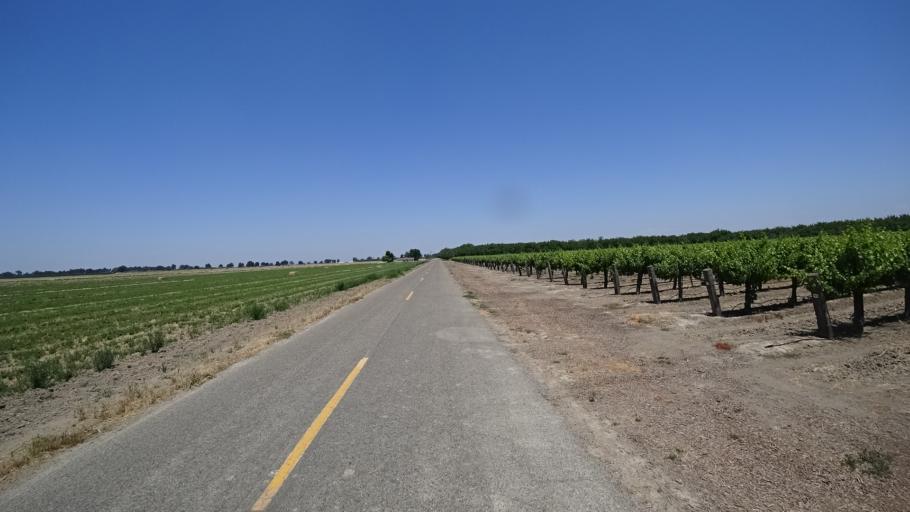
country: US
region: California
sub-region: Fresno County
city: Laton
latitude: 36.4063
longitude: -119.7269
